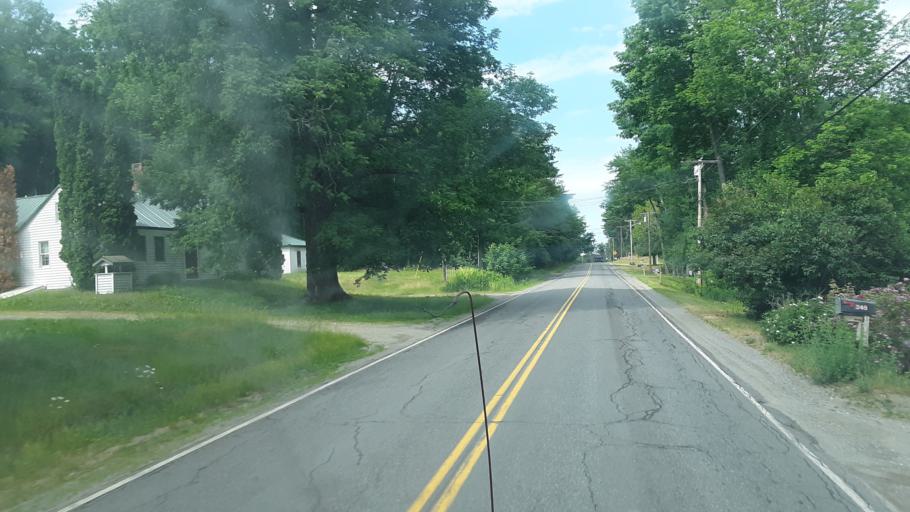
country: US
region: Maine
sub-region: Penobscot County
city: Hampden
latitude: 44.7286
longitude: -68.8728
